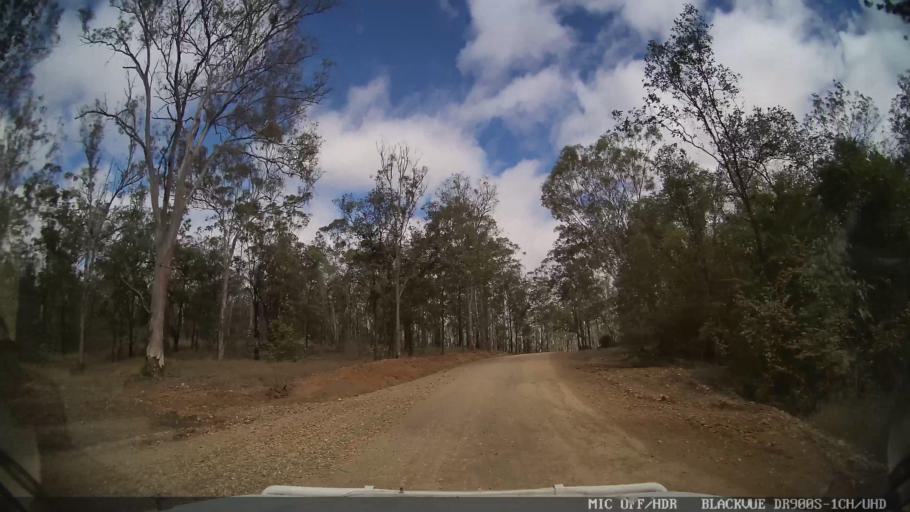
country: AU
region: Queensland
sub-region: Gladstone
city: Toolooa
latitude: -24.6847
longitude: 151.3291
